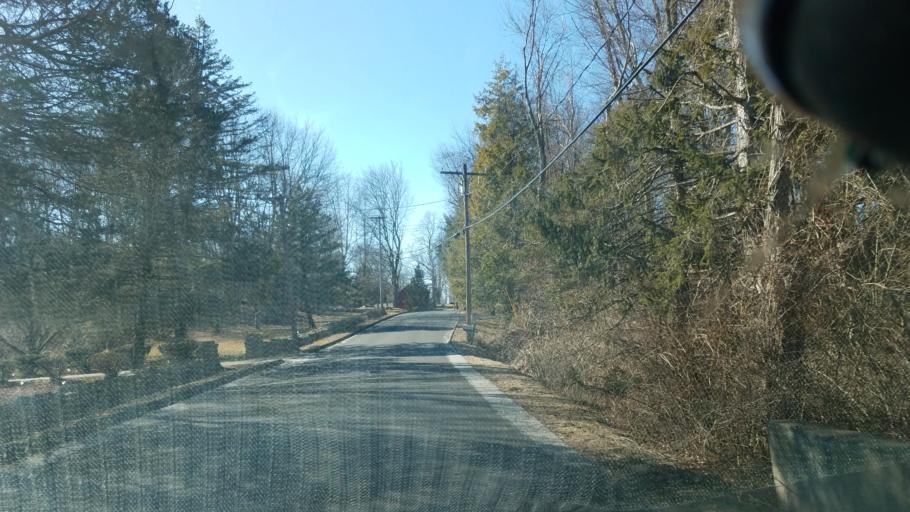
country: US
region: Connecticut
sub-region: Fairfield County
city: Newtown
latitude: 41.3550
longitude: -73.3125
